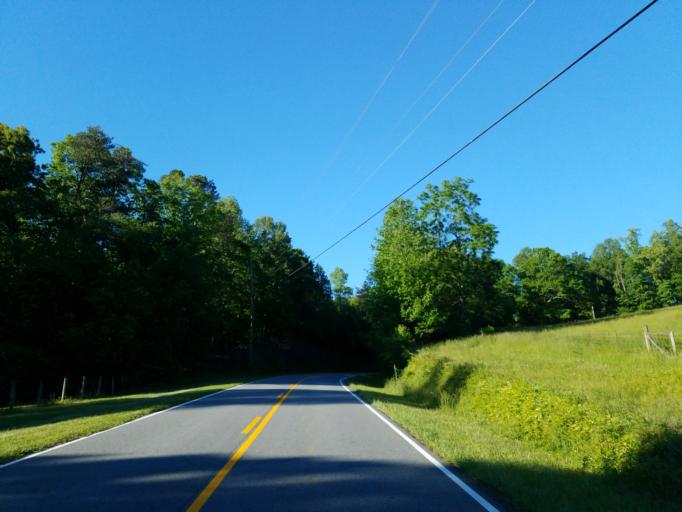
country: US
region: Georgia
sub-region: Gilmer County
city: Ellijay
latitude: 34.6872
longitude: -84.3142
